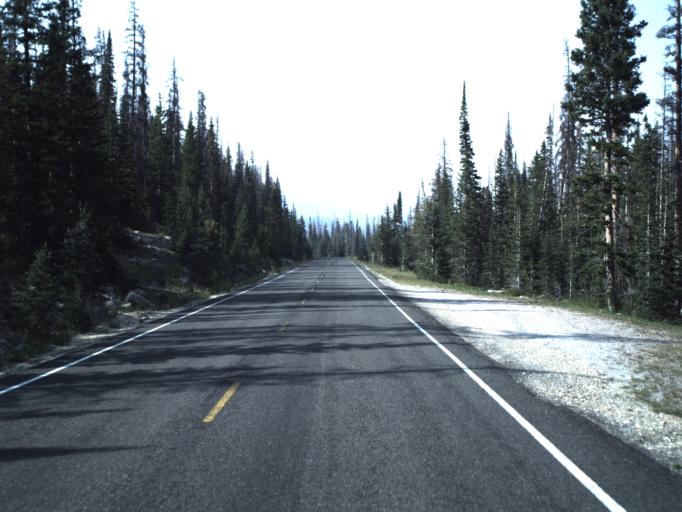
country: US
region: Utah
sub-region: Summit County
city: Kamas
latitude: 40.7425
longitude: -110.8714
